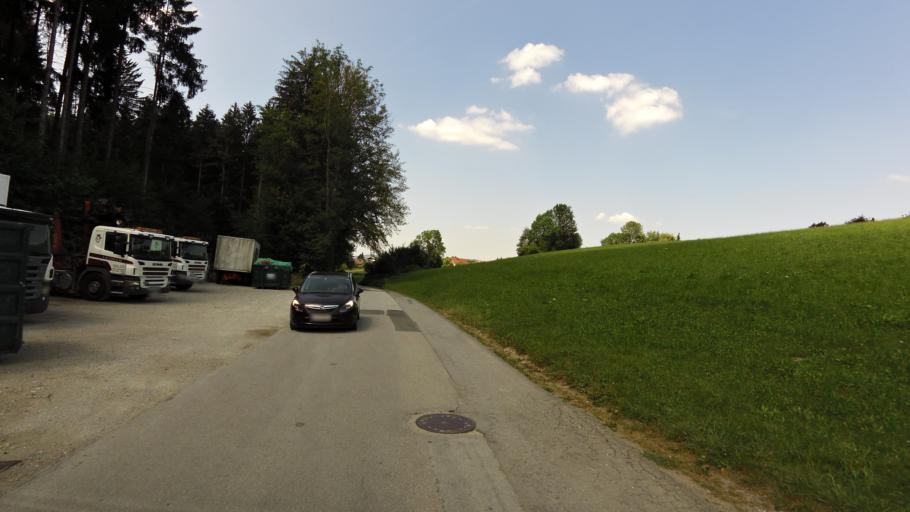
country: AT
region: Salzburg
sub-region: Politischer Bezirk Salzburg-Umgebung
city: Henndorf am Wallersee
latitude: 47.8933
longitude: 13.1922
